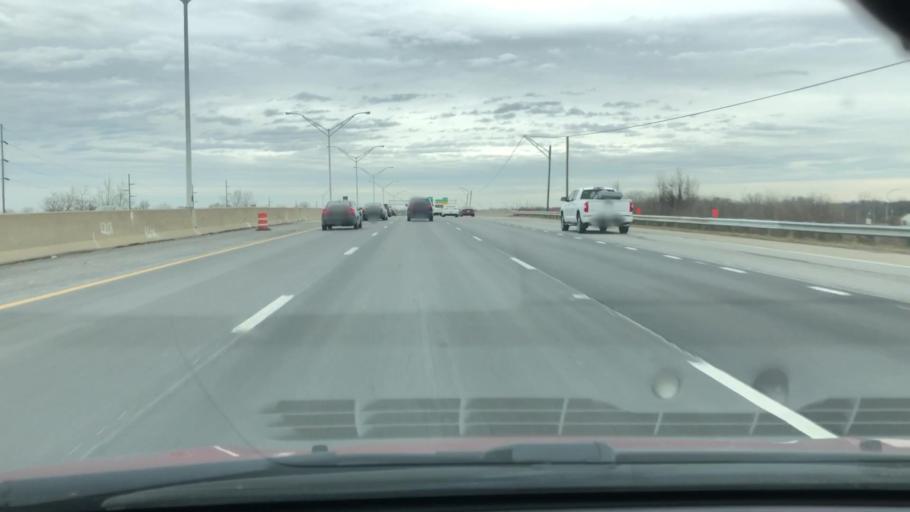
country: US
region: Ohio
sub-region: Franklin County
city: Bexley
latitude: 39.9798
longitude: -82.9647
